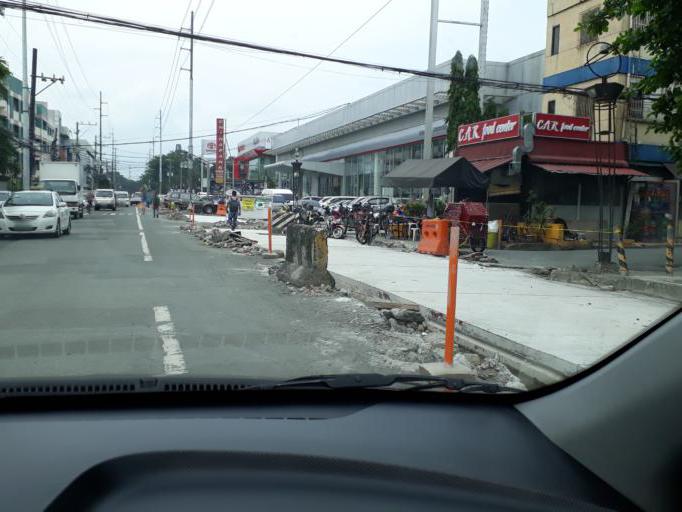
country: PH
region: Metro Manila
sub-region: City of Manila
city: Quiapo
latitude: 14.5888
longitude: 120.9968
